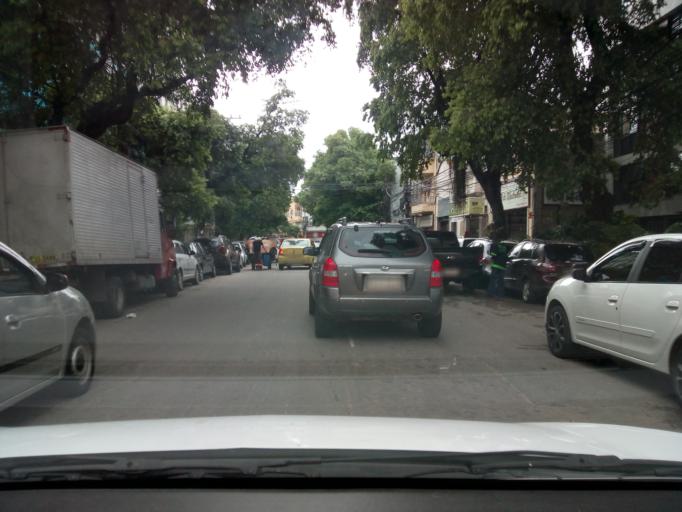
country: BR
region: Rio de Janeiro
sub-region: Rio De Janeiro
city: Rio de Janeiro
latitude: -22.9021
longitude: -43.2177
